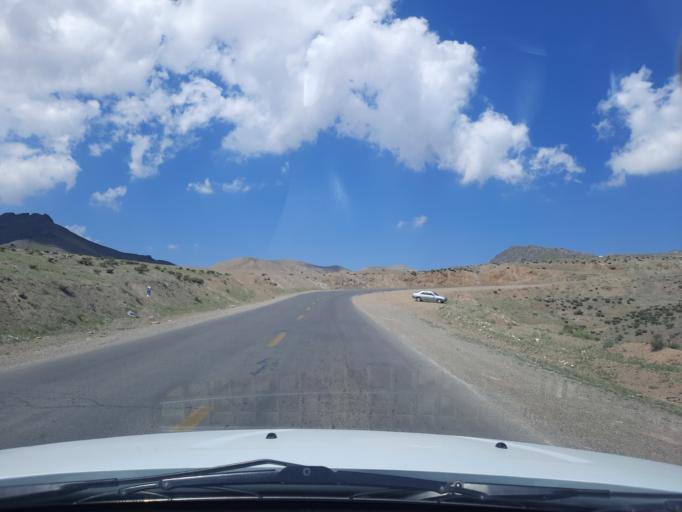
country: IR
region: Qazvin
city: Qazvin
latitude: 36.3560
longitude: 50.1902
